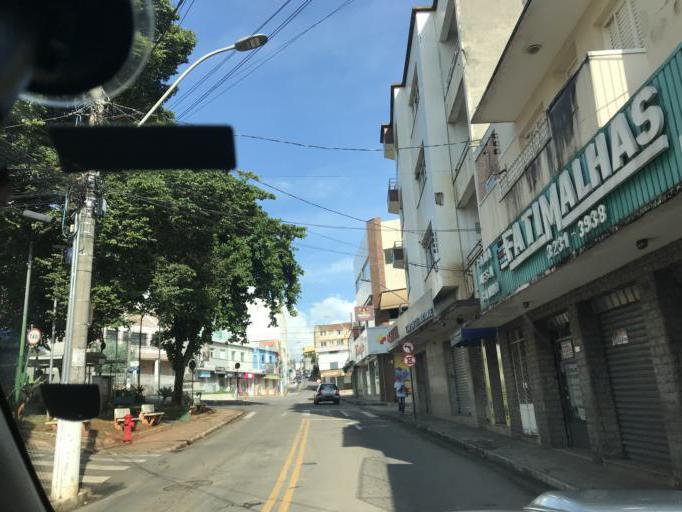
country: BR
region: Minas Gerais
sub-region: Tres Coracoes
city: Tres Coracoes
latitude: -21.6949
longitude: -45.2575
